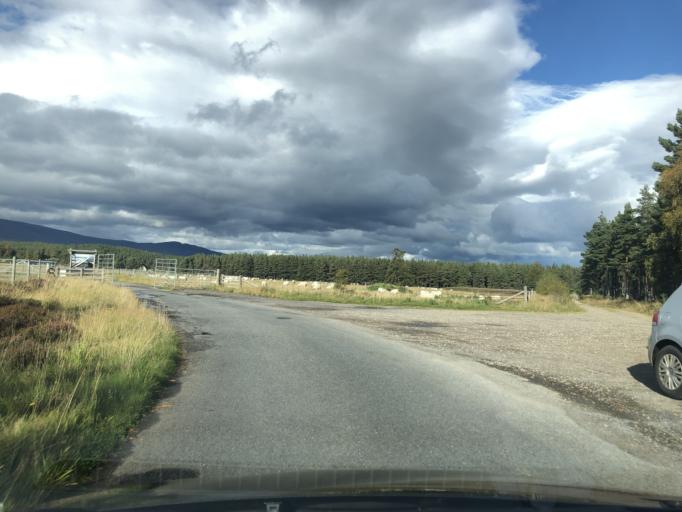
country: GB
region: Scotland
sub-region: Highland
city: Aviemore
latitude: 57.1056
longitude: -3.8871
